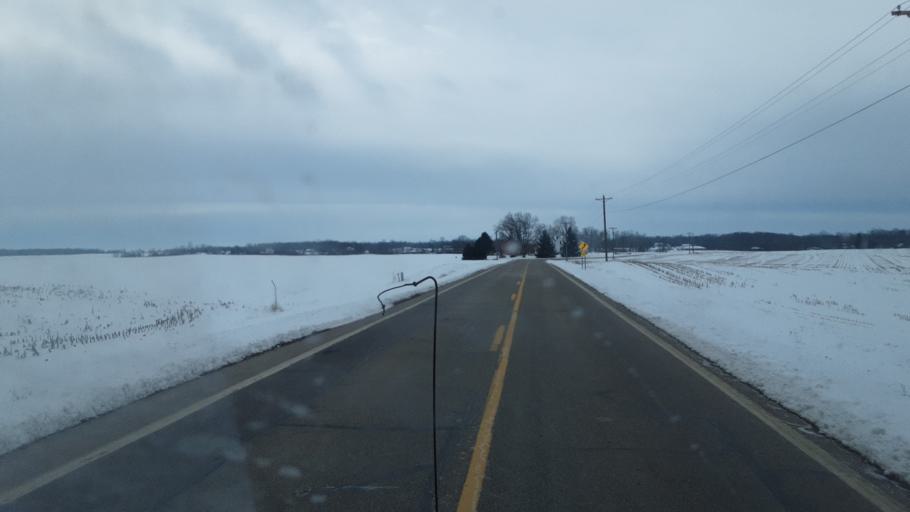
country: US
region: Ohio
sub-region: Champaign County
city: Mechanicsburg
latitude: 40.0470
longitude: -83.5325
